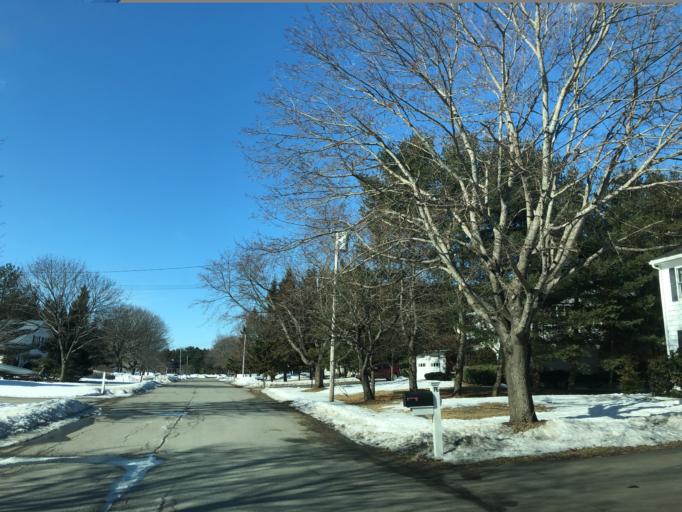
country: US
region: Maine
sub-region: Penobscot County
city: Brewer
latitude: 44.8209
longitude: -68.7465
